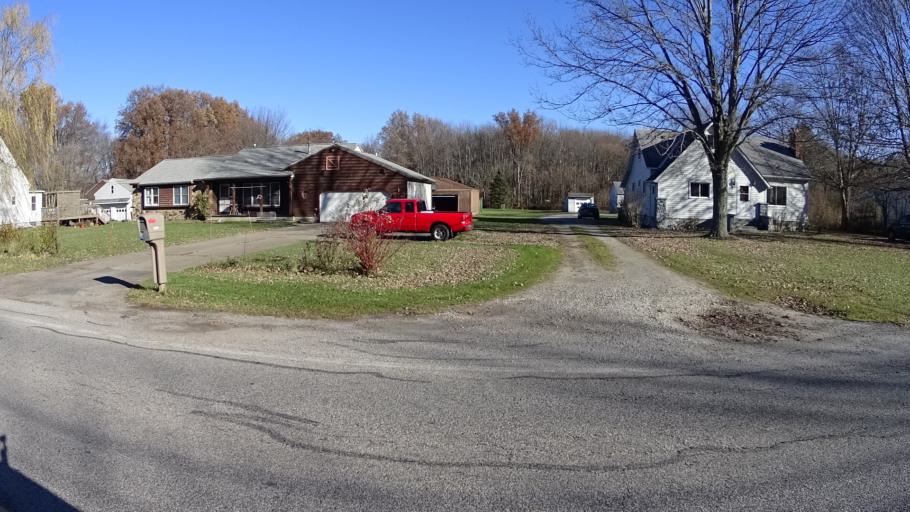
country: US
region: Ohio
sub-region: Lorain County
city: North Ridgeville
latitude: 41.3974
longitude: -82.0188
